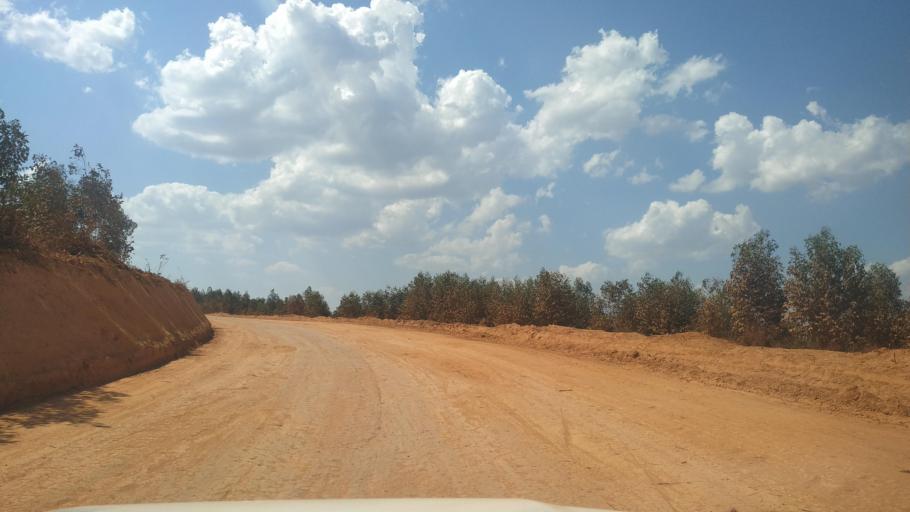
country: MG
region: Alaotra Mangoro
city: Ambatondrazaka
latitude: -18.0819
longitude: 48.2591
